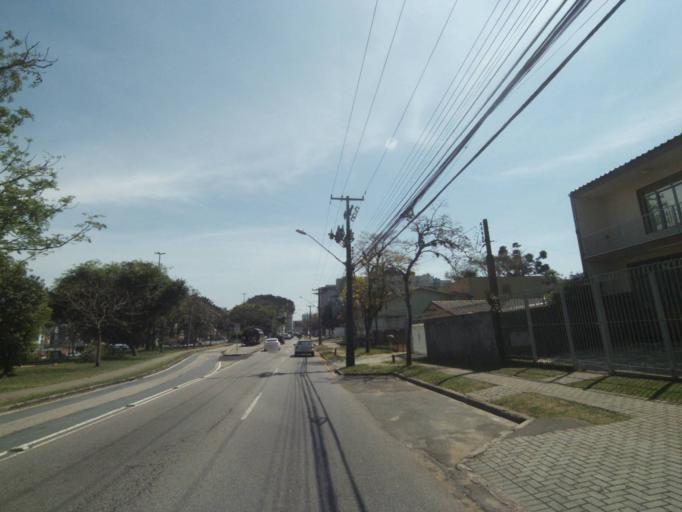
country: BR
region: Parana
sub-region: Curitiba
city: Curitiba
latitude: -25.4772
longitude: -49.2844
